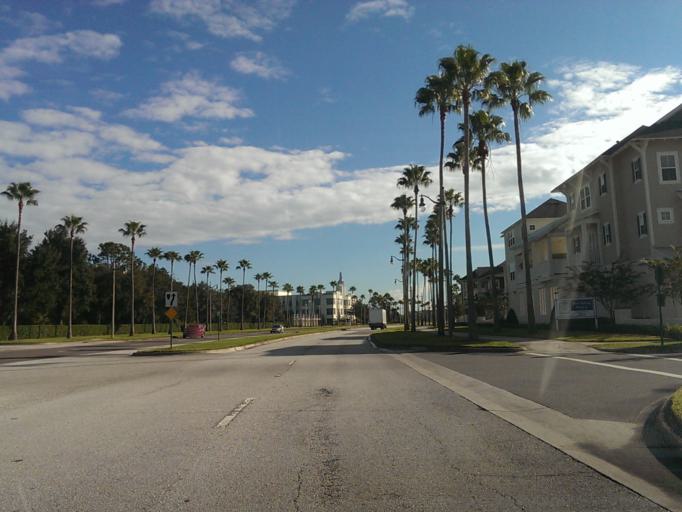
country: US
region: Florida
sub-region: Osceola County
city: Celebration
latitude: 28.3120
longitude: -81.5622
